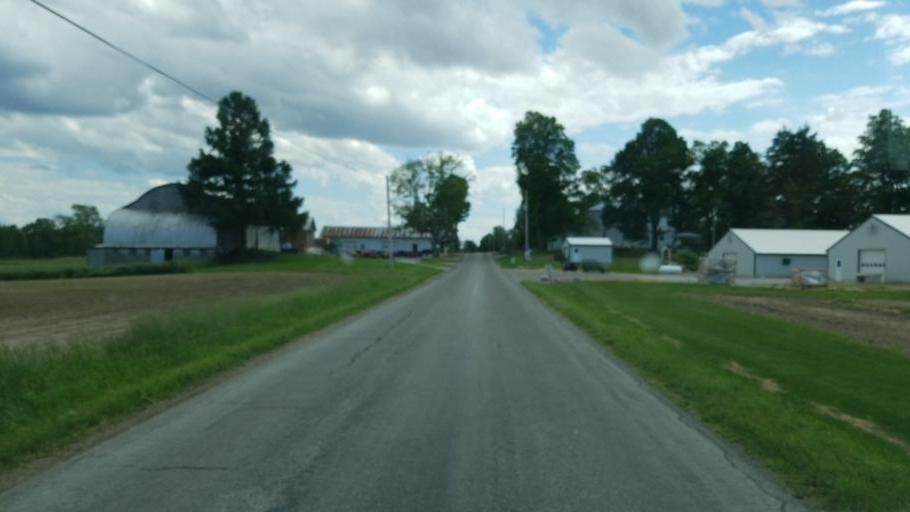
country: US
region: Ohio
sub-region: Huron County
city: Plymouth
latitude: 40.9802
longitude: -82.6061
